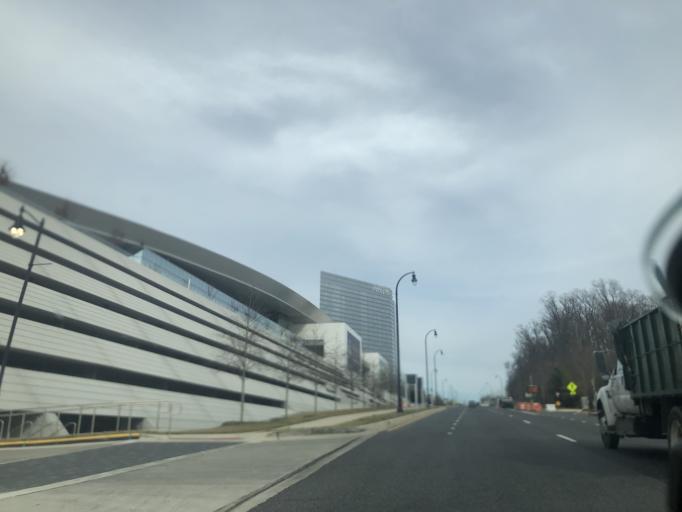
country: US
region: Maryland
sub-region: Prince George's County
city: Forest Heights
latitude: 38.7927
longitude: -77.0088
